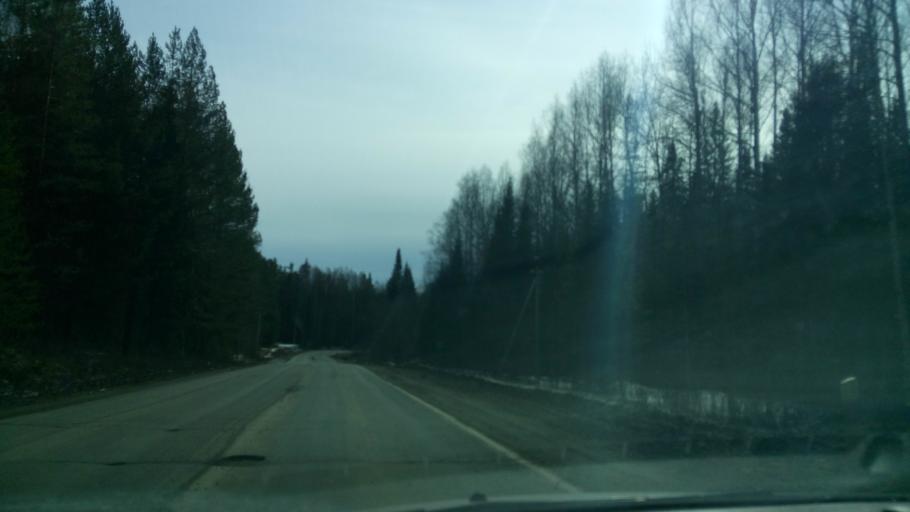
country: RU
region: Sverdlovsk
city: Chernoistochinsk
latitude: 57.7206
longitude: 59.7844
